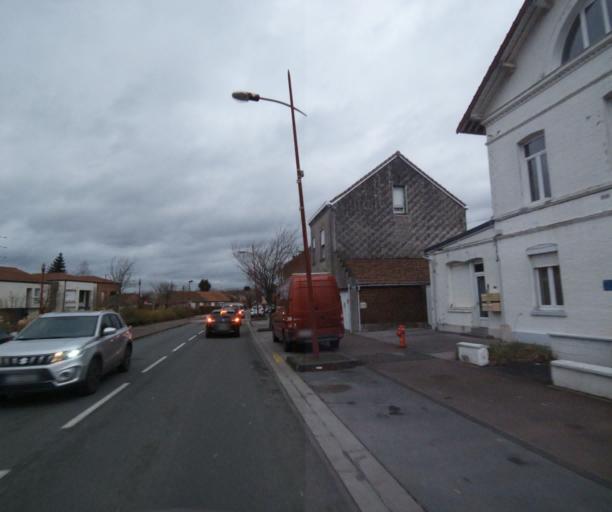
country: FR
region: Nord-Pas-de-Calais
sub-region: Departement du Nord
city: Anzin
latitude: 50.3811
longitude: 3.5104
